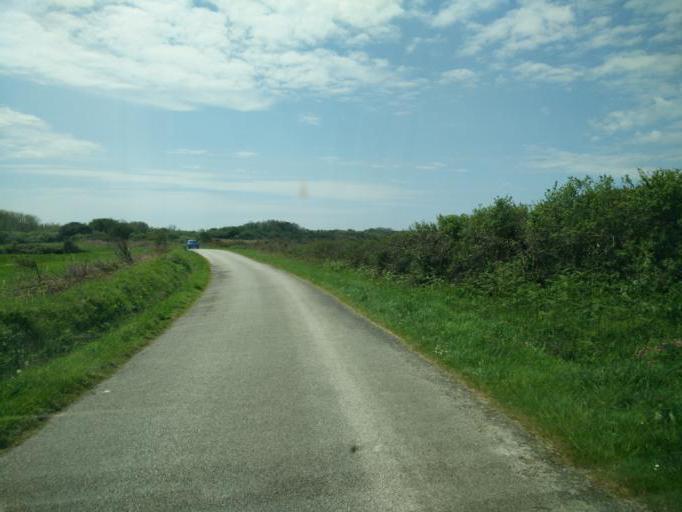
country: FR
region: Brittany
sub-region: Departement du Finistere
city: Roscanvel
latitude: 48.3321
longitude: -4.5612
